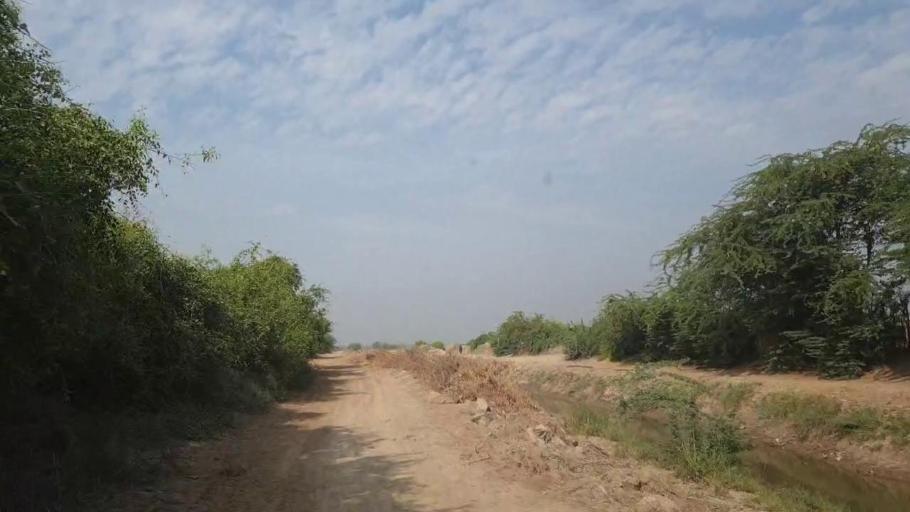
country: PK
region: Sindh
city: Tando Bago
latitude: 24.8823
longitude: 68.9355
